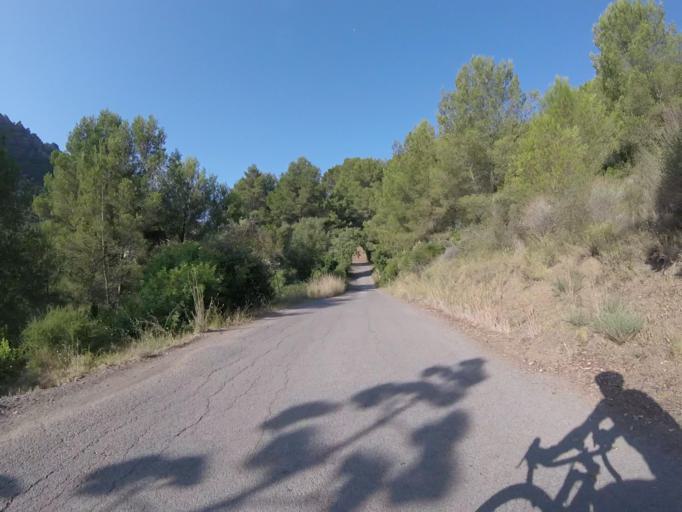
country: ES
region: Valencia
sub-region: Provincia de Castello
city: Benicassim
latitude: 40.0838
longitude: 0.0533
